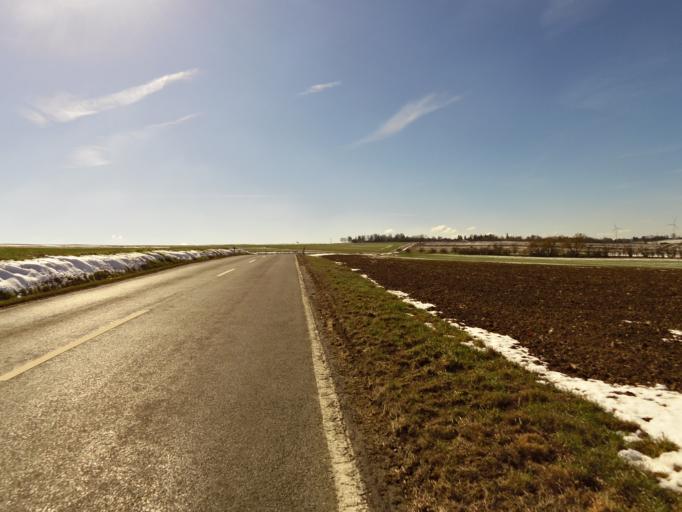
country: DE
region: Rheinland-Pfalz
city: Ottersheim
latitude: 49.6167
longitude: 8.1145
